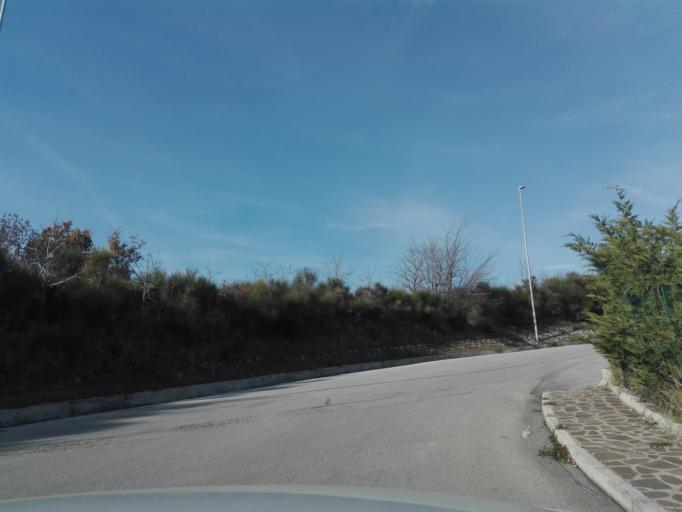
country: IT
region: Molise
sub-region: Provincia di Isernia
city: Agnone
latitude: 41.8157
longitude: 14.3699
